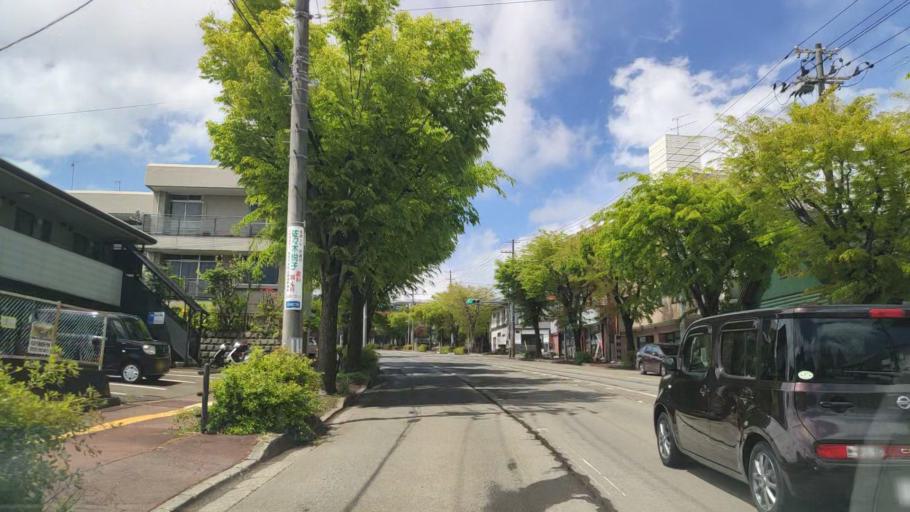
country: JP
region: Miyagi
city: Sendai
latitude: 38.2402
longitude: 140.8464
